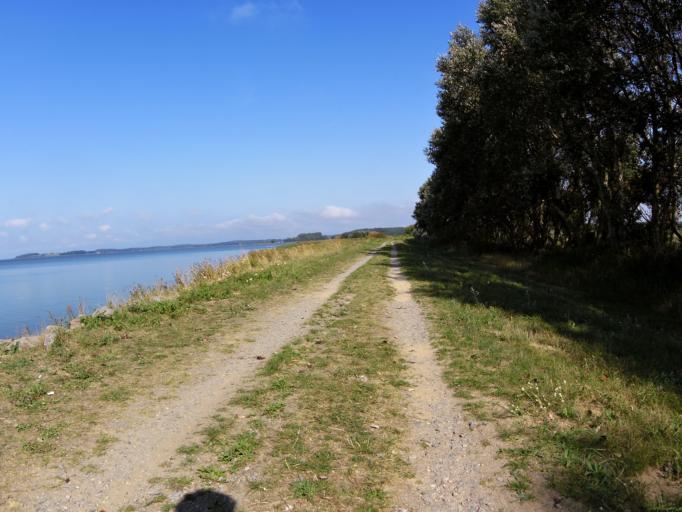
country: DE
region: Mecklenburg-Vorpommern
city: Loddin
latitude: 53.9837
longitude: 14.0485
